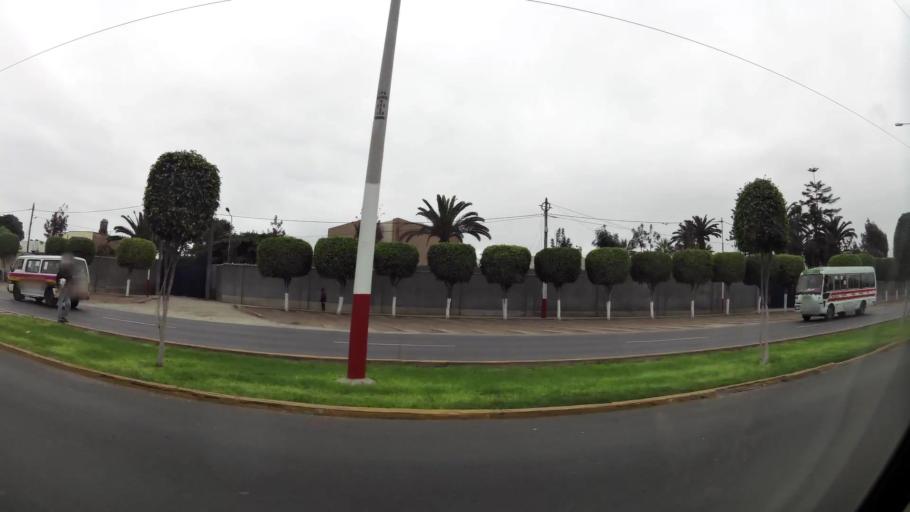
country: PE
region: Callao
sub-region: Callao
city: Callao
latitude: -12.0581
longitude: -77.1203
